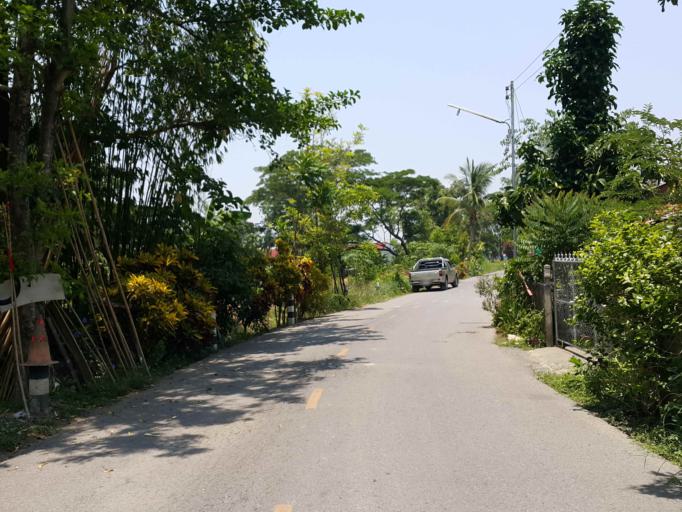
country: TH
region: Chiang Mai
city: San Kamphaeng
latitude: 18.7995
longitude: 99.1120
